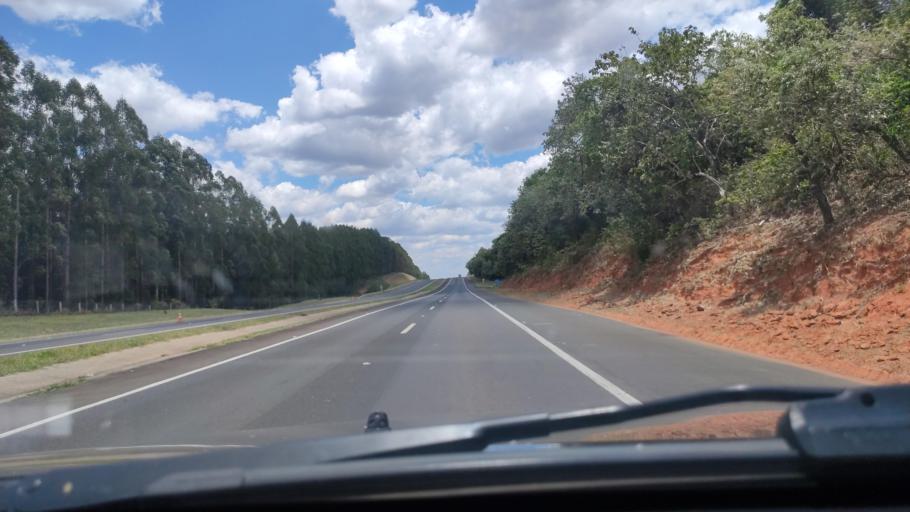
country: BR
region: Sao Paulo
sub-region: Duartina
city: Duartina
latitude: -22.4883
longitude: -49.2443
